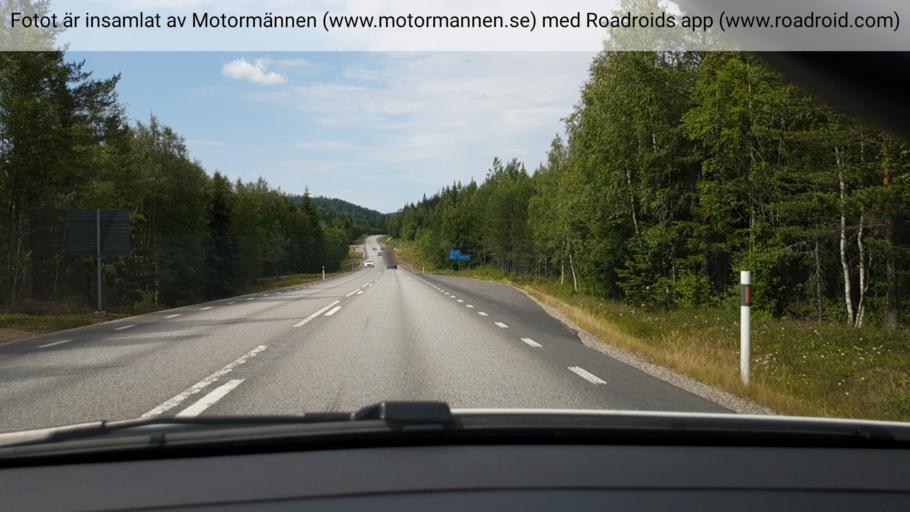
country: SE
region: Dalarna
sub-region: Faluns Kommun
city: Bjursas
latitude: 60.7910
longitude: 15.2793
